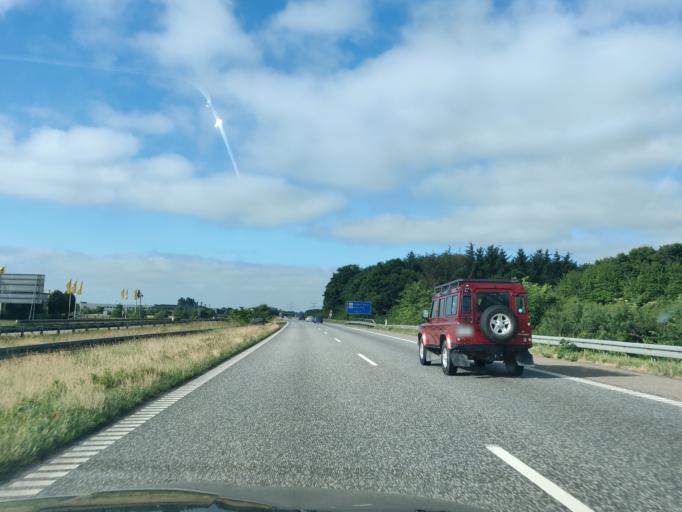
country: DK
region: North Denmark
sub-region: Rebild Kommune
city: Stovring
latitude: 56.8889
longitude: 9.8106
